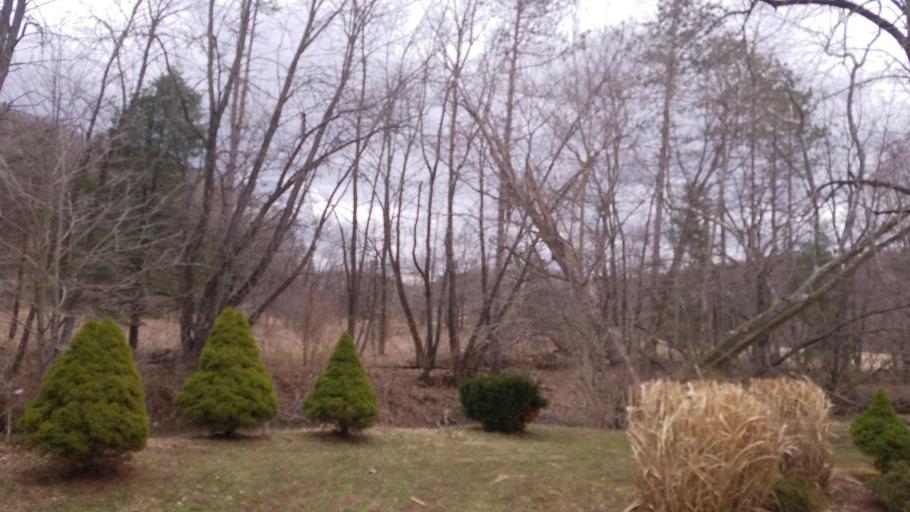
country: US
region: Ohio
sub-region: Licking County
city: Newark
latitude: 40.1678
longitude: -82.2957
